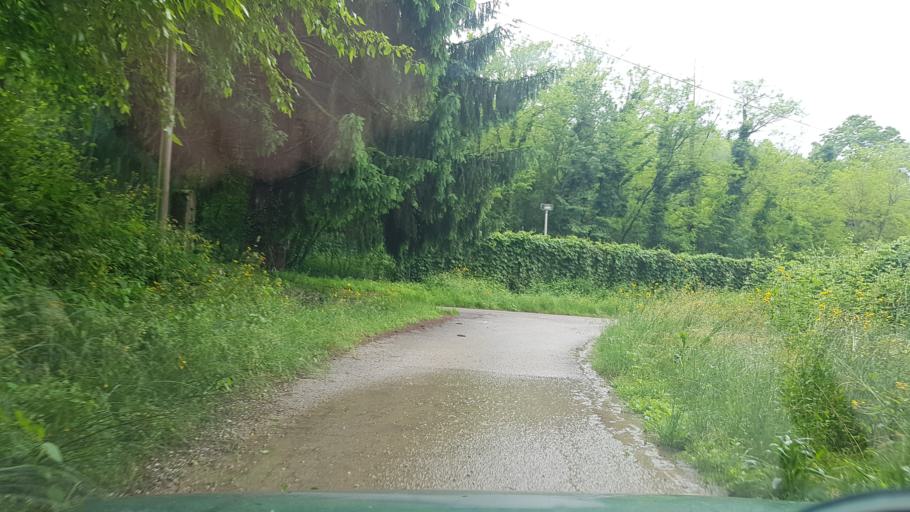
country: IT
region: Friuli Venezia Giulia
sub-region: Provincia di Gorizia
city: Mossa
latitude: 45.9453
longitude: 13.5815
